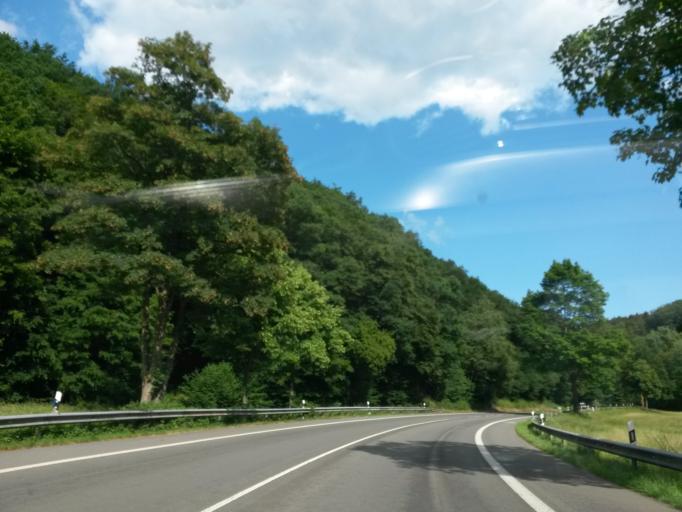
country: DE
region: North Rhine-Westphalia
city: Lohmar
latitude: 50.8458
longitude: 7.2491
